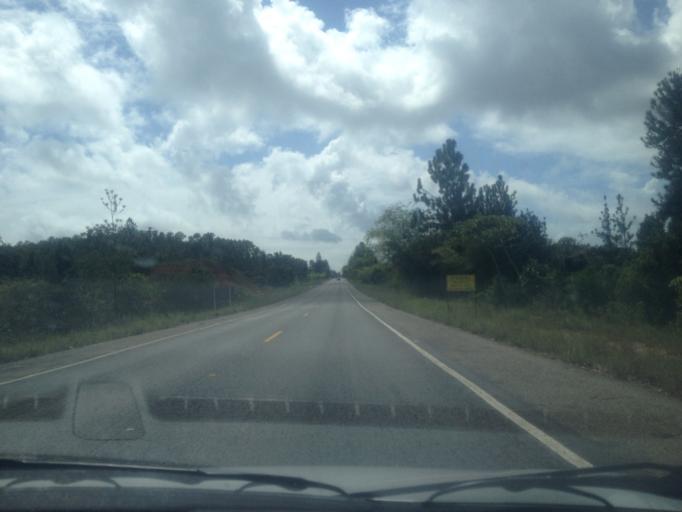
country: BR
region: Bahia
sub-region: Conde
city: Conde
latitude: -12.0137
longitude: -37.6885
